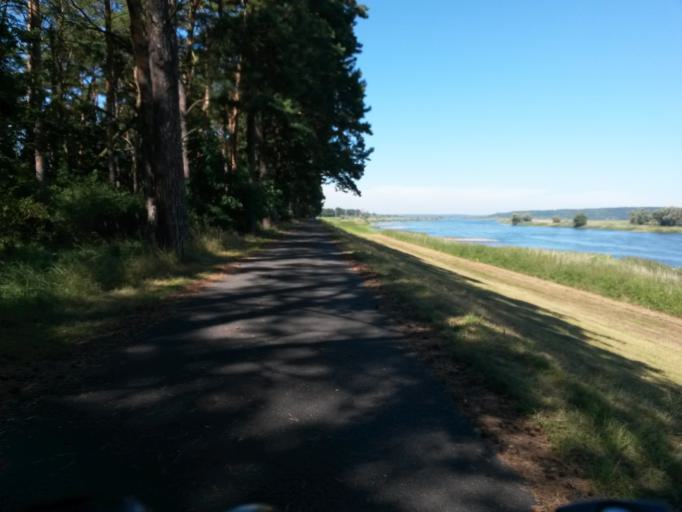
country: PL
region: West Pomeranian Voivodeship
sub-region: Powiat gryfinski
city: Cedynia
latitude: 52.8932
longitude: 14.1553
